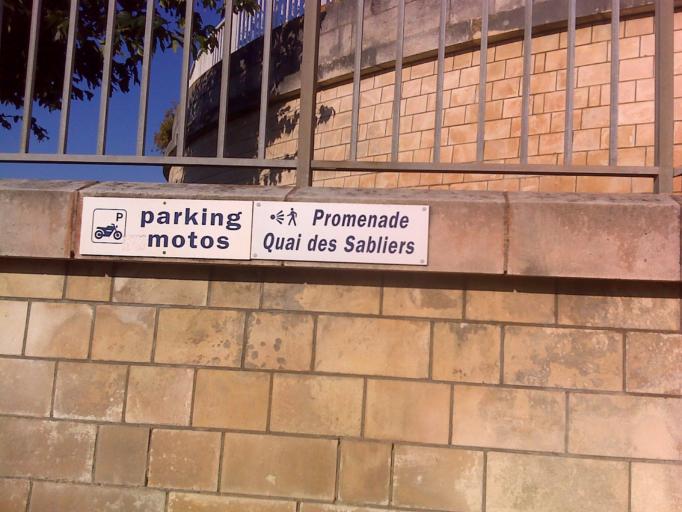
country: FR
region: Poitou-Charentes
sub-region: Departement de la Charente-Maritime
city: Royan
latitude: 45.6191
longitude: -1.0317
